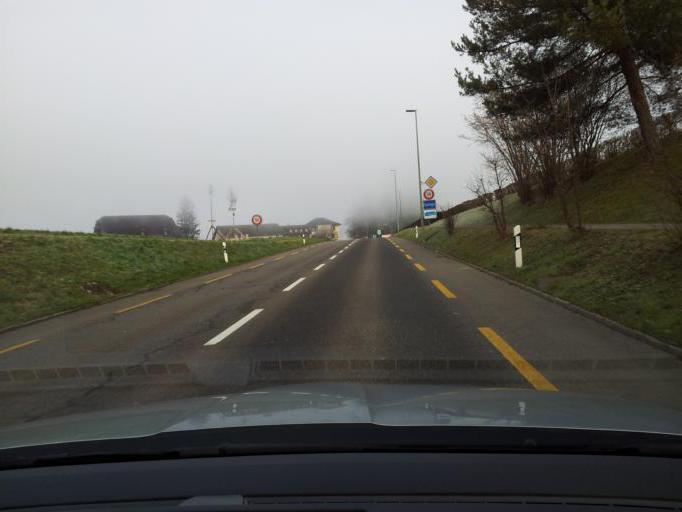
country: CH
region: Obwalden
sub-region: Obwalden
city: Sarnen
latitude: 46.8867
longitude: 8.2459
